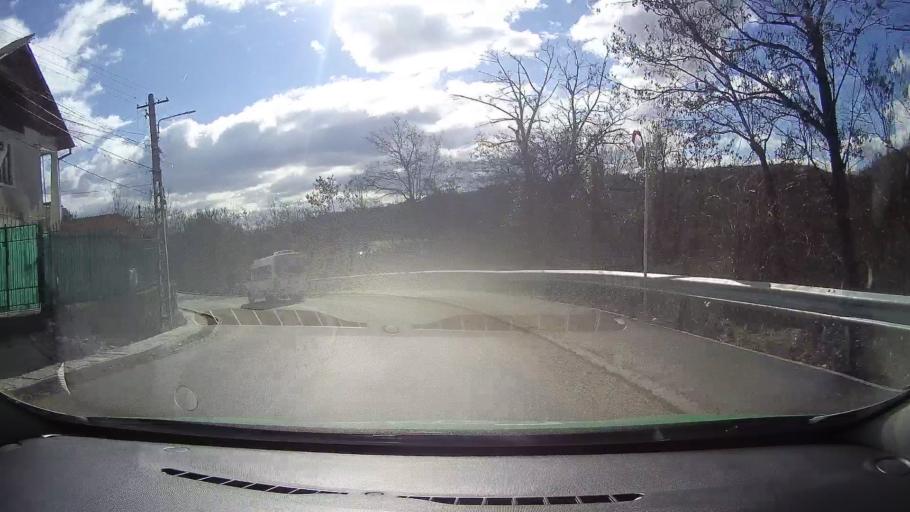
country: RO
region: Dambovita
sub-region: Comuna Fieni
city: Fieni
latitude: 45.1324
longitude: 25.4041
